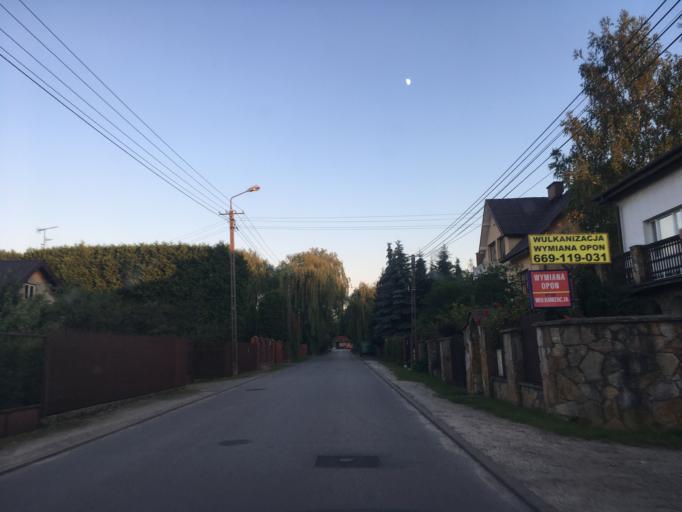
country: PL
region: Masovian Voivodeship
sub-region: Powiat piaseczynski
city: Piaseczno
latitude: 52.0668
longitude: 21.0113
